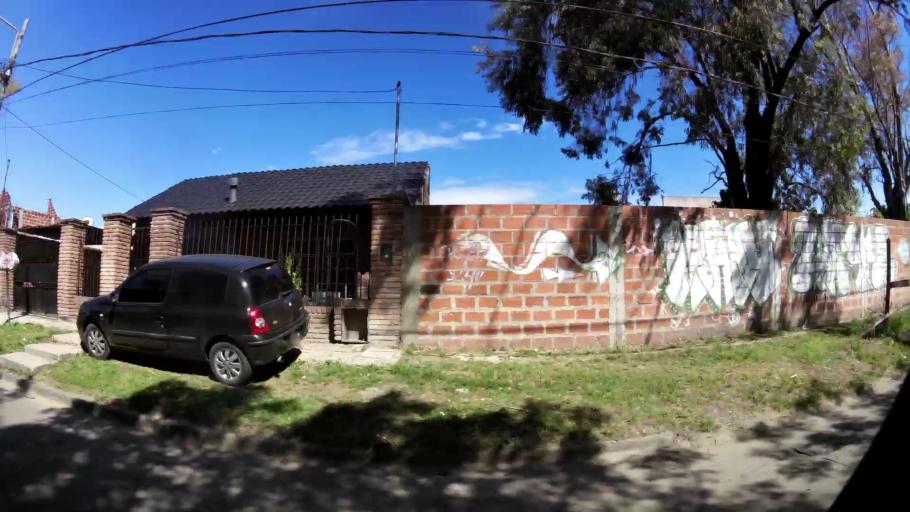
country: AR
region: Buenos Aires
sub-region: Partido de Almirante Brown
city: Adrogue
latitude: -34.7876
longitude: -58.3592
